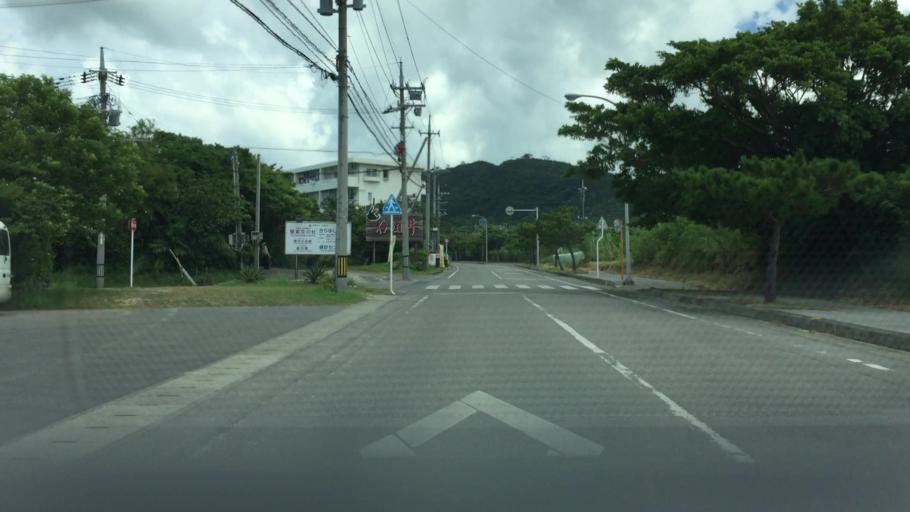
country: JP
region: Okinawa
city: Ishigaki
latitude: 24.3613
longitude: 124.1434
